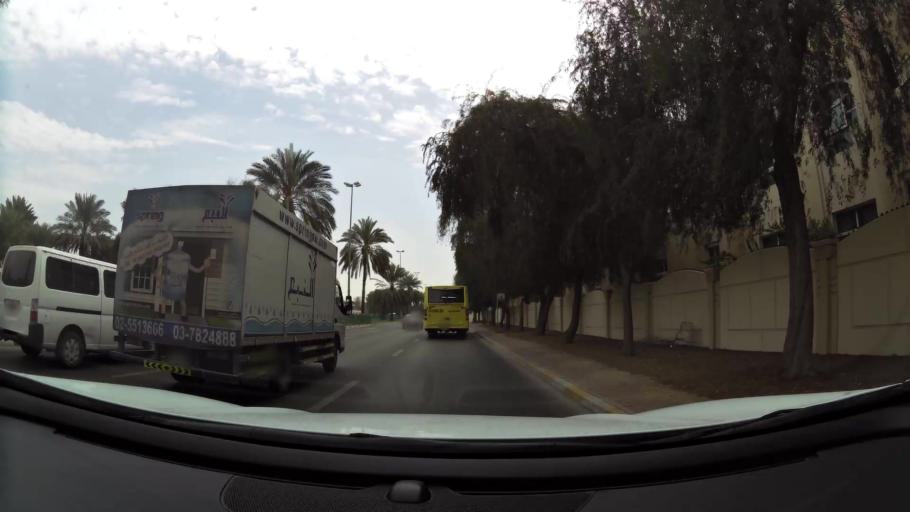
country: OM
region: Al Buraimi
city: Al Buraymi
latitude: 24.2202
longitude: 55.7854
